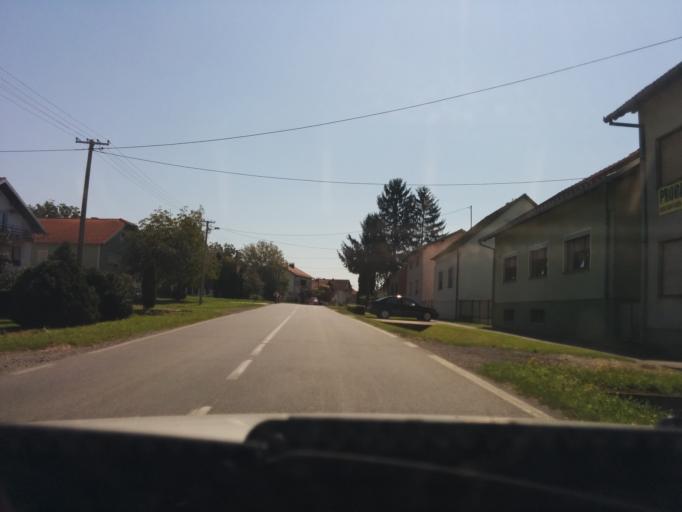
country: HR
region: Sisacko-Moslavacka
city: Novska
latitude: 45.3594
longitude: 16.9536
